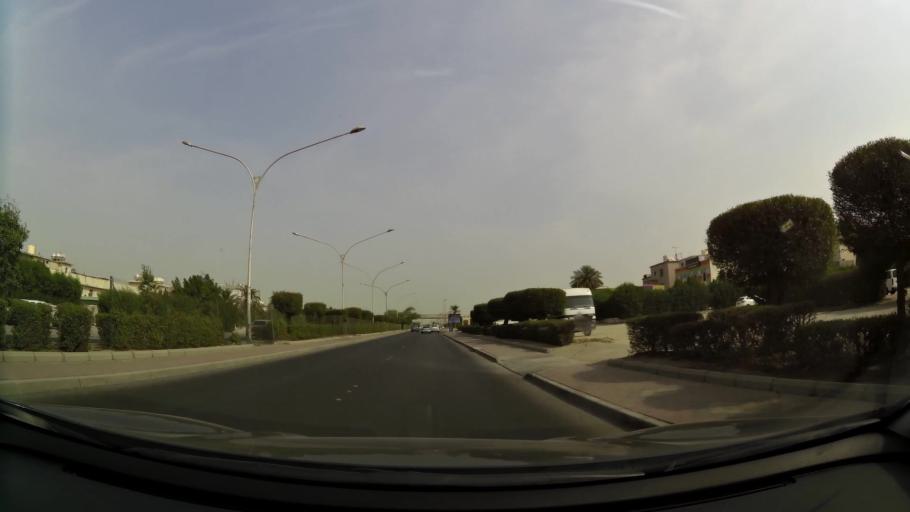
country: KW
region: Al Asimah
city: Ar Rabiyah
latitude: 29.2887
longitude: 47.9367
